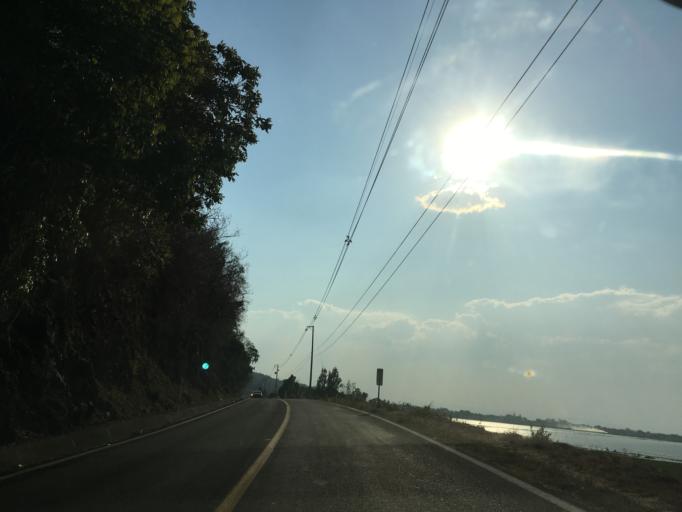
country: MX
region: Michoacan
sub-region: Zinapecuaro
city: Santa Clara del Tule
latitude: 19.8088
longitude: -100.8575
